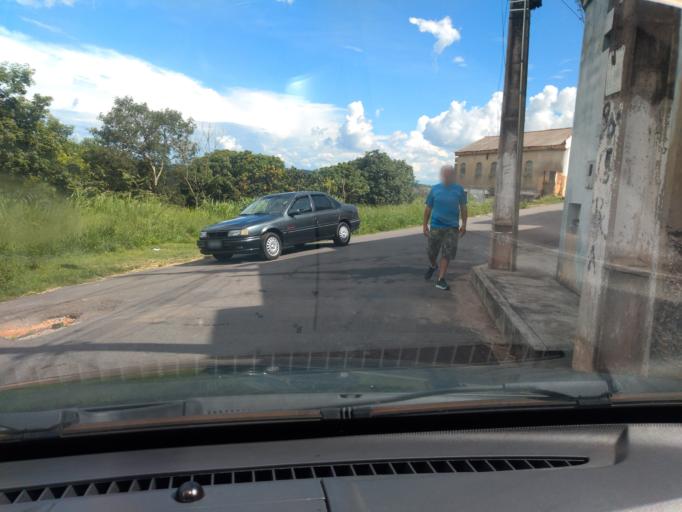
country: BR
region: Minas Gerais
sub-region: Tres Coracoes
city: Tres Coracoes
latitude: -21.6958
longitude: -45.2487
